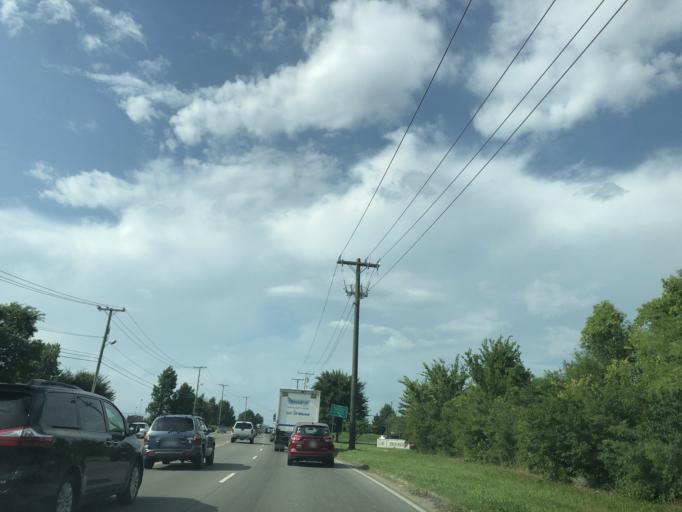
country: US
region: Tennessee
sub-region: Davidson County
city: Oak Hill
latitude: 36.1017
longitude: -86.6751
